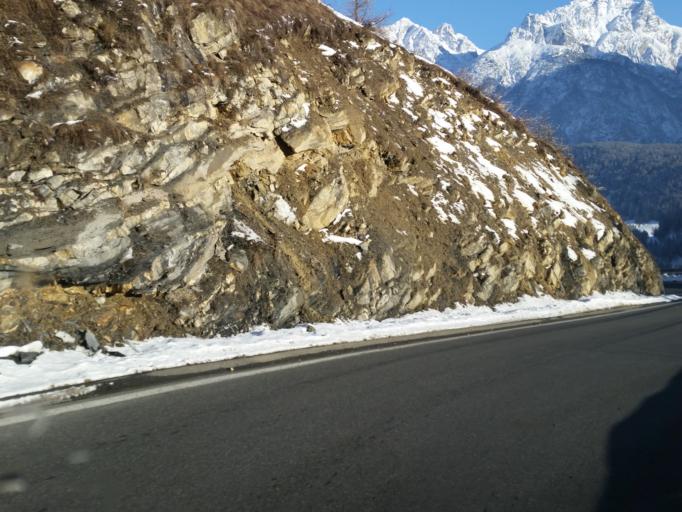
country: CH
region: Grisons
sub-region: Inn District
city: Scuol
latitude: 46.7911
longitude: 10.2593
